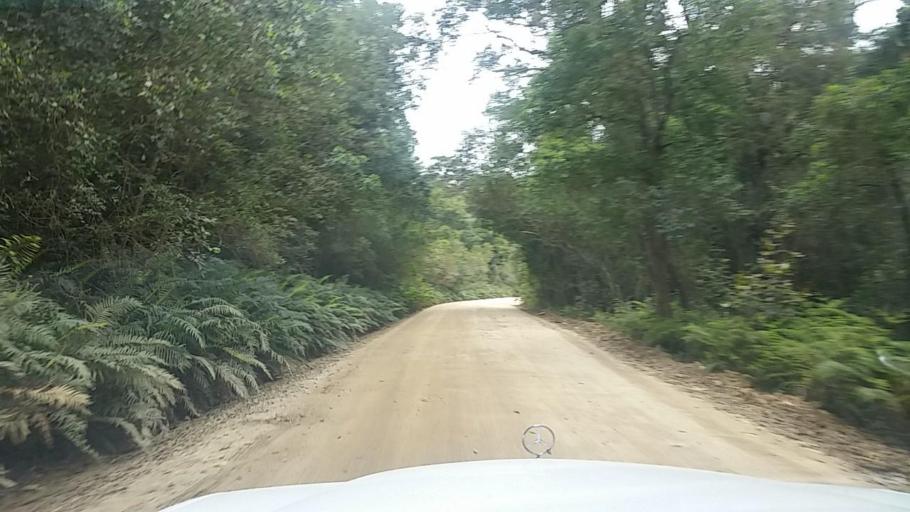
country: ZA
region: Western Cape
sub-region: Eden District Municipality
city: Knysna
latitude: -33.9548
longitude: 23.1517
